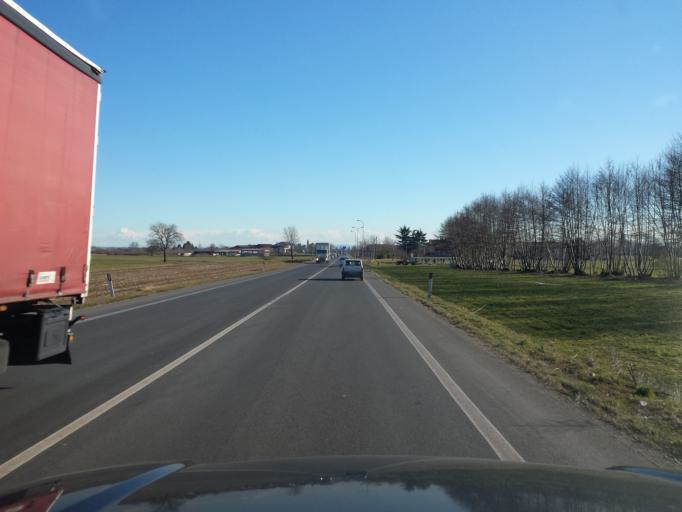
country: IT
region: Piedmont
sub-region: Provincia di Torino
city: Ozegna
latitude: 45.3617
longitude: 7.7284
